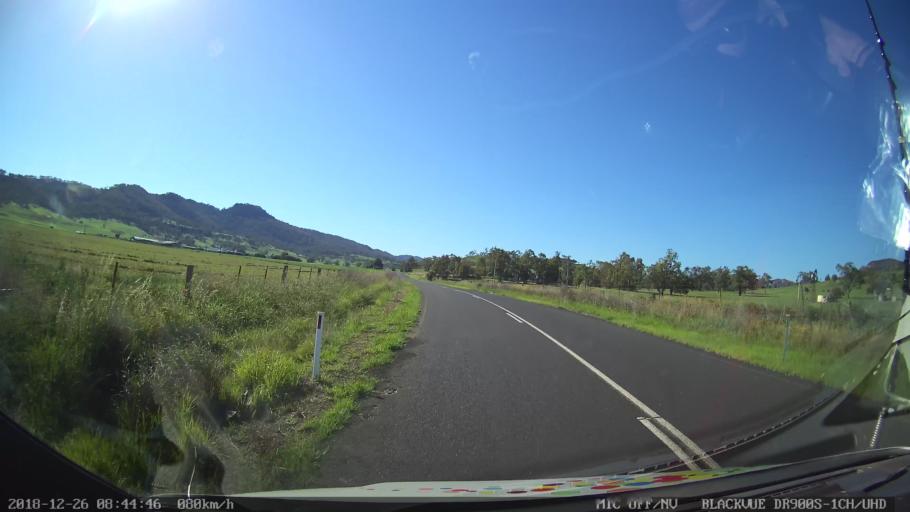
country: AU
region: New South Wales
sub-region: Mid-Western Regional
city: Kandos
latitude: -32.5185
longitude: 150.0814
